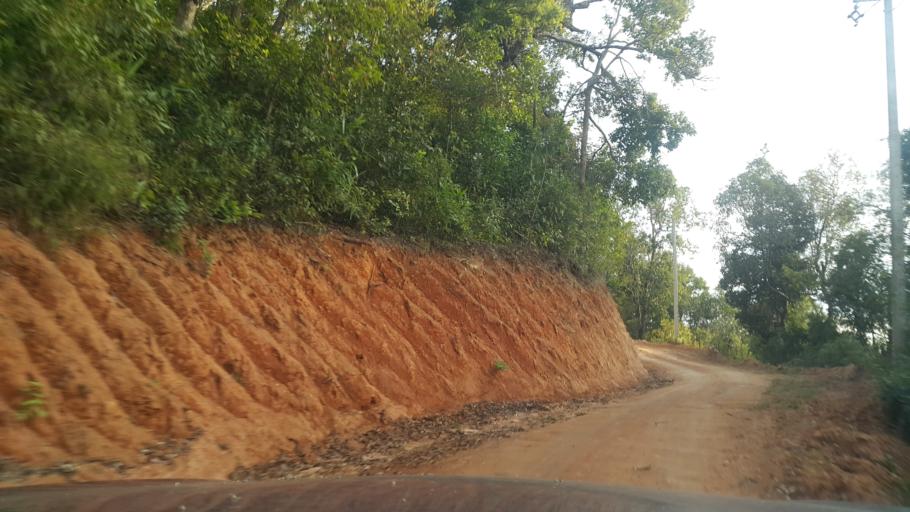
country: TH
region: Chiang Mai
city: Samoeng
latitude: 19.0041
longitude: 98.6481
